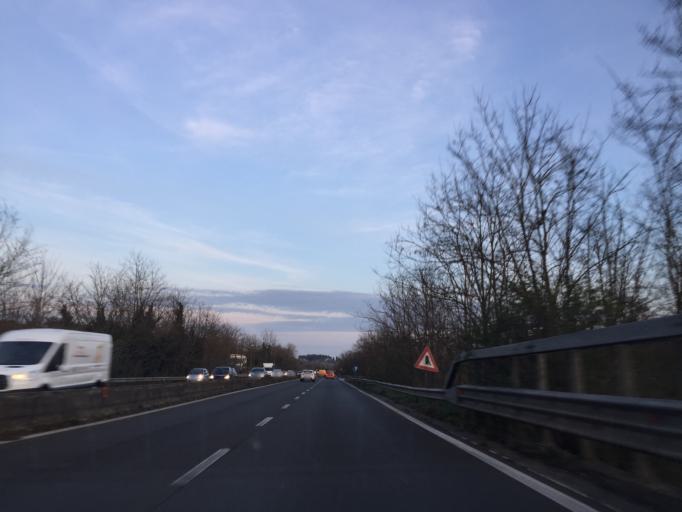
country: IT
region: Latium
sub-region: Citta metropolitana di Roma Capitale
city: Monte Caminetto
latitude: 41.9988
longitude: 12.4540
